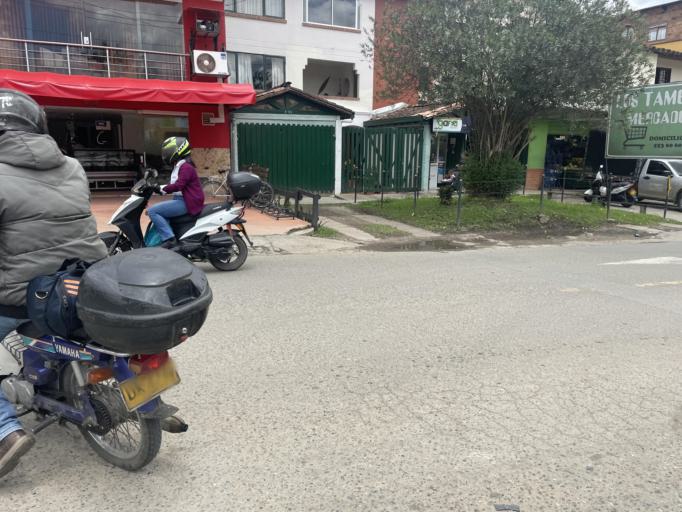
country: CO
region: Antioquia
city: La Ceja
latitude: 6.0219
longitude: -75.4333
